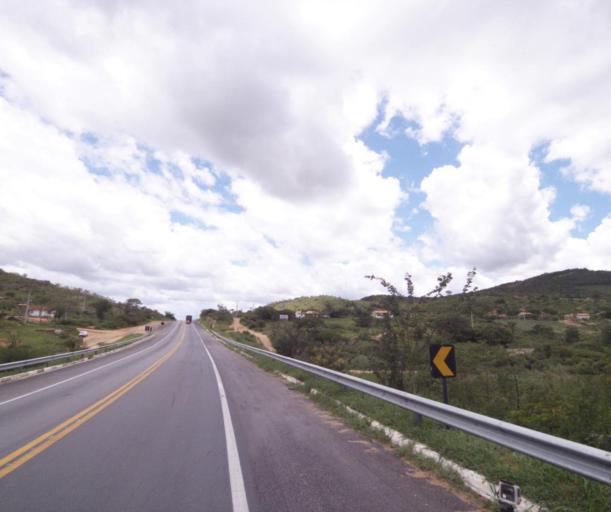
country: BR
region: Bahia
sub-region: Pocoes
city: Pocoes
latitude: -14.3612
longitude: -40.3398
